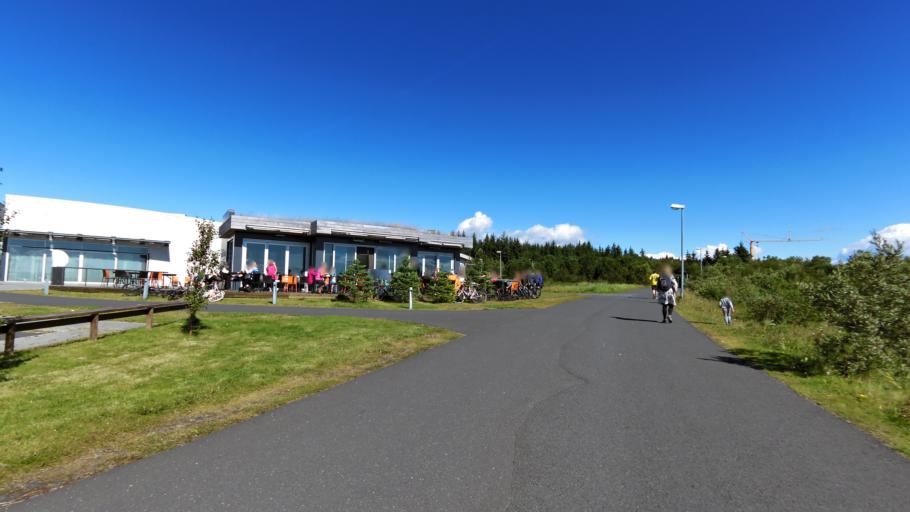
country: IS
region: Capital Region
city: Kopavogur
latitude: 64.1223
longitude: -21.9261
